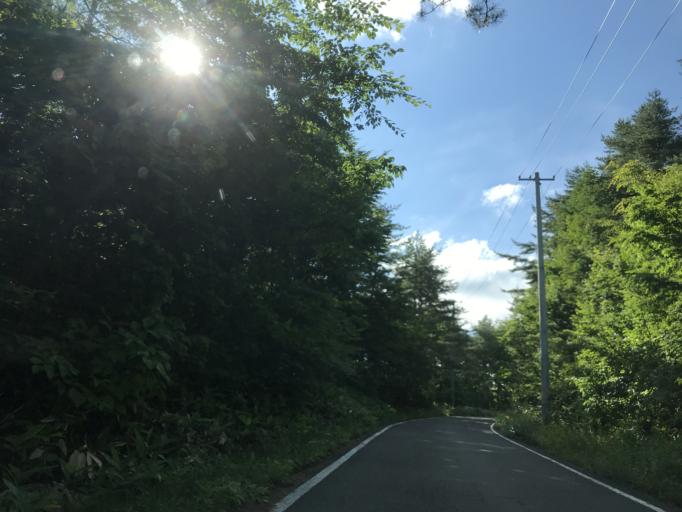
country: JP
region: Iwate
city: Ichinoseki
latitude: 38.8939
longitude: 140.8910
